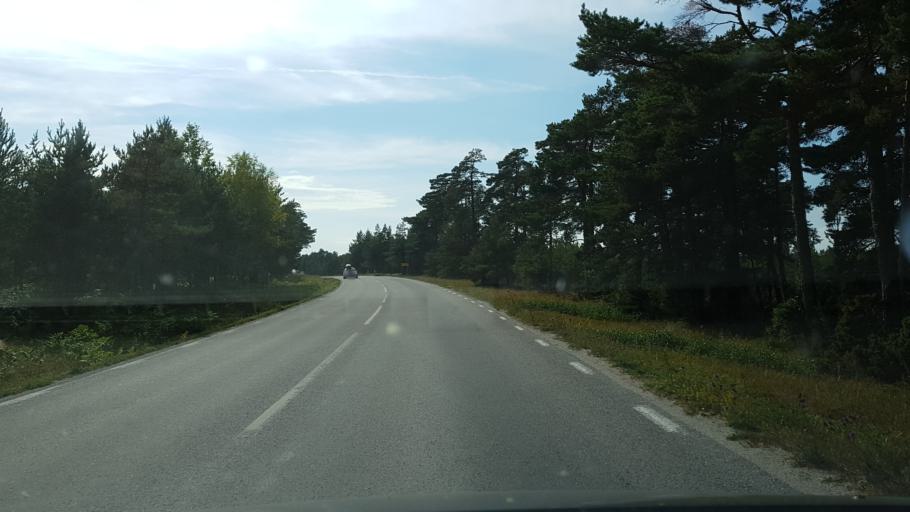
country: SE
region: Gotland
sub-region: Gotland
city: Visby
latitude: 57.6380
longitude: 18.3975
